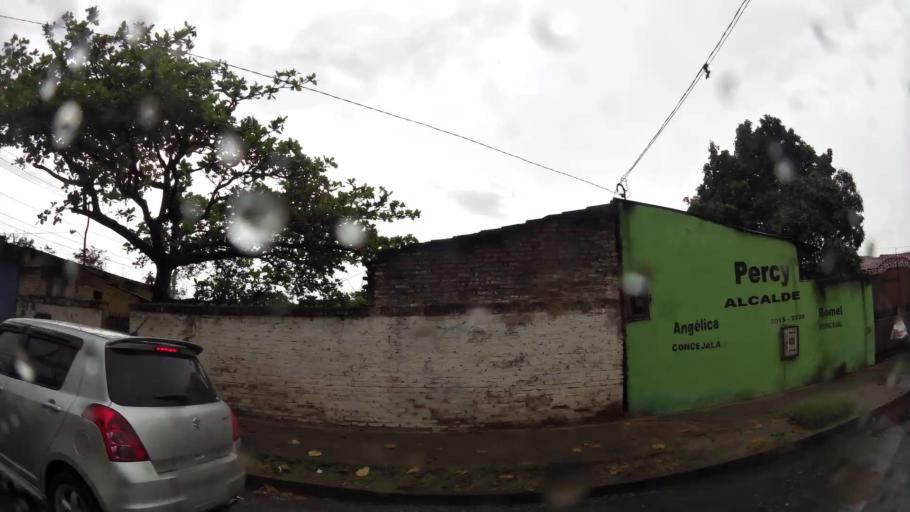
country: BO
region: Santa Cruz
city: Santa Cruz de la Sierra
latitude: -17.7947
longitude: -63.1571
